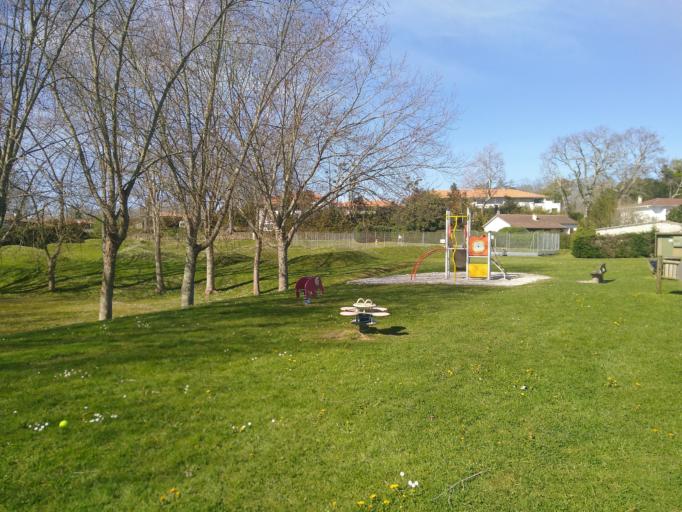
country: FR
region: Aquitaine
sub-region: Departement des Landes
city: Saint-Martin-de-Seignanx
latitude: 43.5430
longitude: -1.3909
